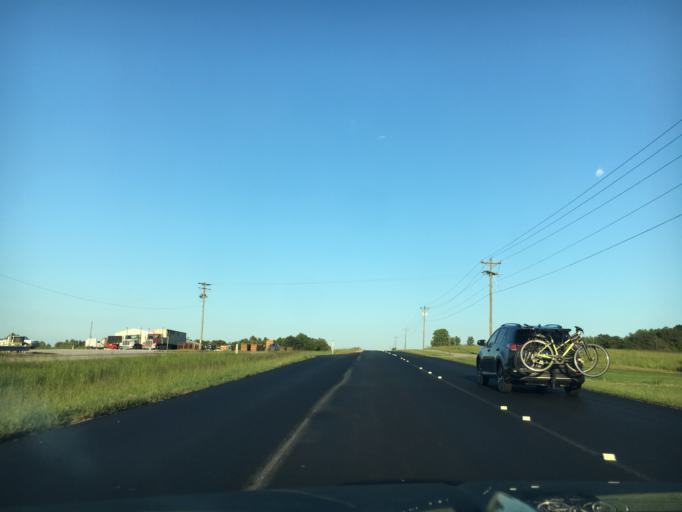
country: US
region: Virginia
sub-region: City of Danville
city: Danville
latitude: 36.5806
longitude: -79.2467
